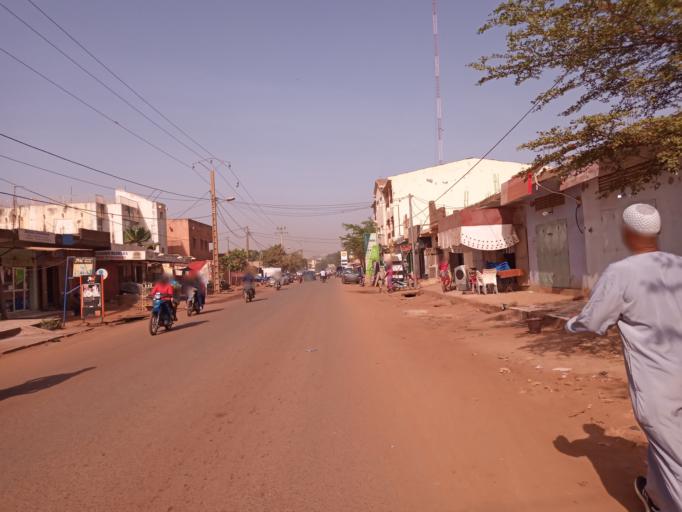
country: ML
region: Bamako
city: Bamako
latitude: 12.5884
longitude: -7.9756
